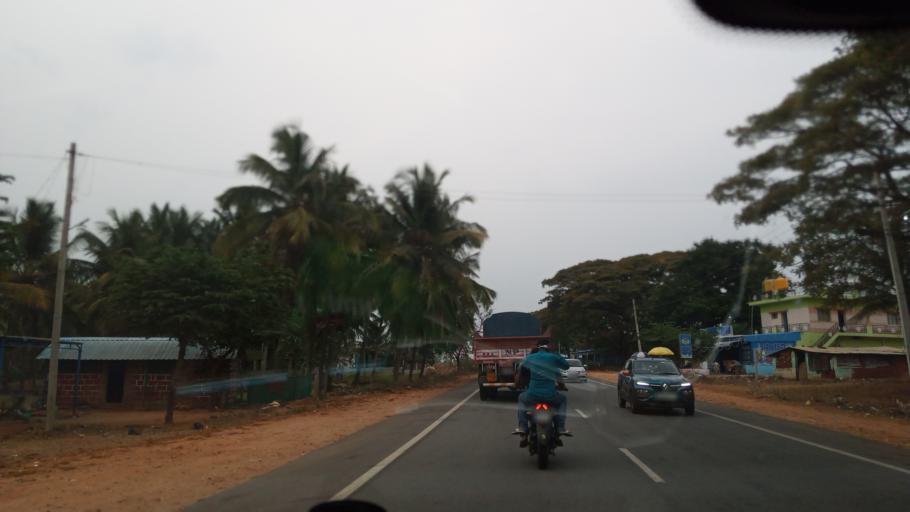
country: IN
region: Karnataka
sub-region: Mandya
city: Nagamangala
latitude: 12.7892
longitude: 76.7501
